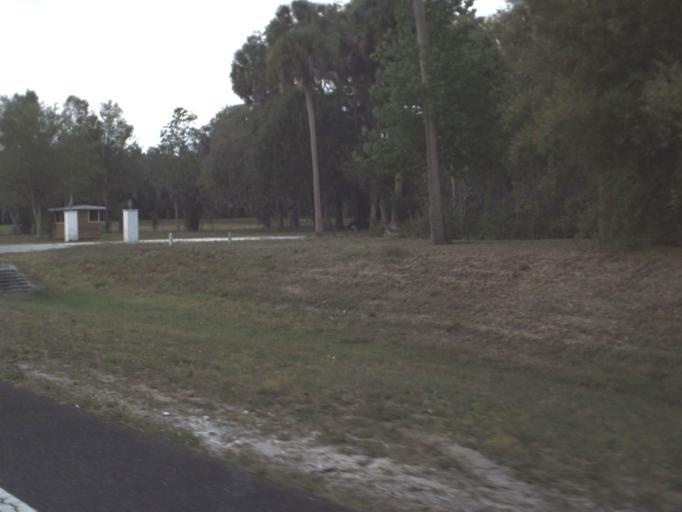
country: US
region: Florida
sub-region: Citrus County
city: Inverness
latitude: 28.8532
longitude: -82.2127
